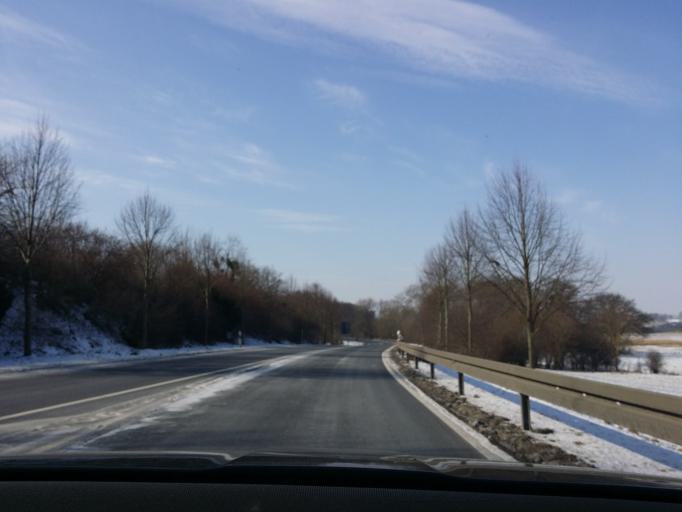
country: DE
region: Mecklenburg-Vorpommern
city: Penzlin
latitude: 53.5083
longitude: 13.0968
